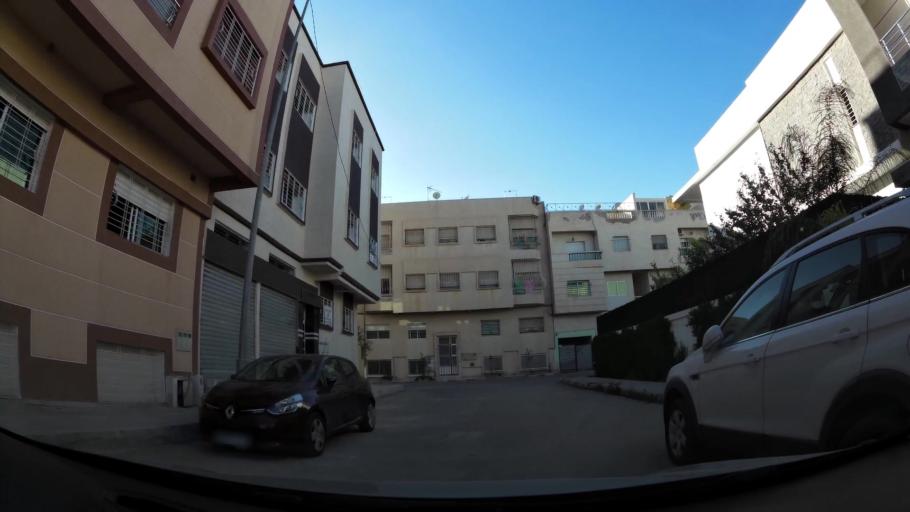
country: MA
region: Fes-Boulemane
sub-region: Fes
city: Fes
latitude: 34.0105
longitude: -5.0124
